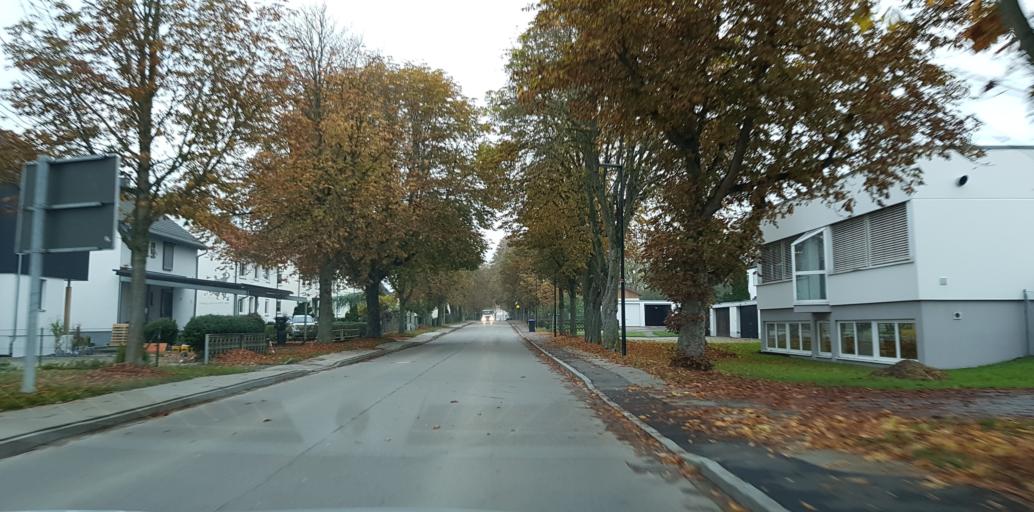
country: DE
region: Baden-Wuerttemberg
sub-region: Tuebingen Region
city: Oberdischingen
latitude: 48.3016
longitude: 9.8399
